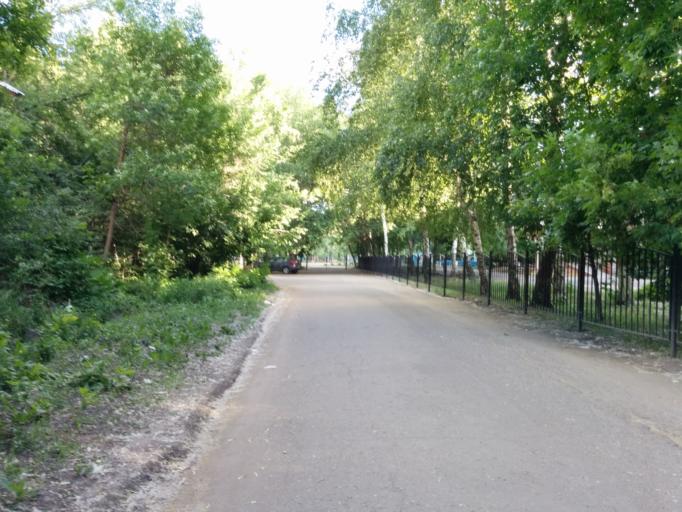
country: RU
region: Tambov
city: Tambov
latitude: 52.7476
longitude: 41.4411
